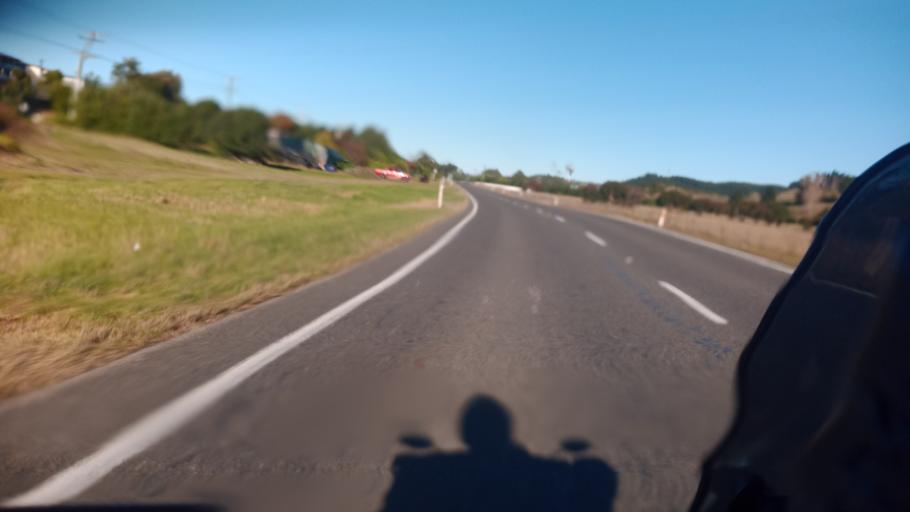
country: NZ
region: Hawke's Bay
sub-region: Napier City
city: Napier
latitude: -39.3673
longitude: 176.8980
